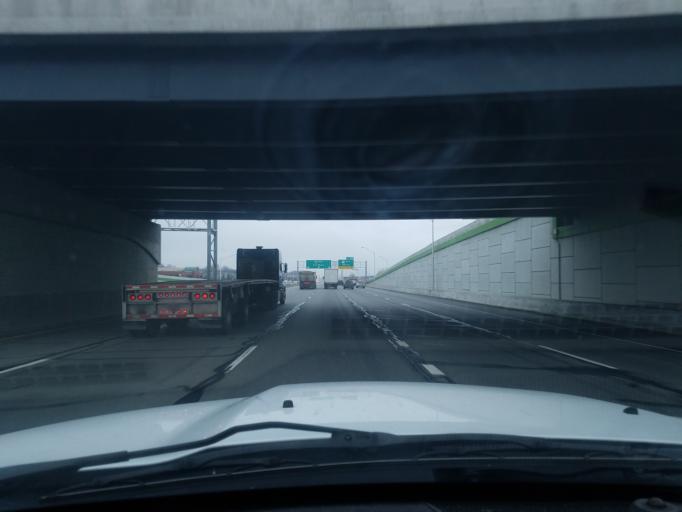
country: US
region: Indiana
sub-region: Hamilton County
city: Fishers
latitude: 39.9421
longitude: -86.0186
